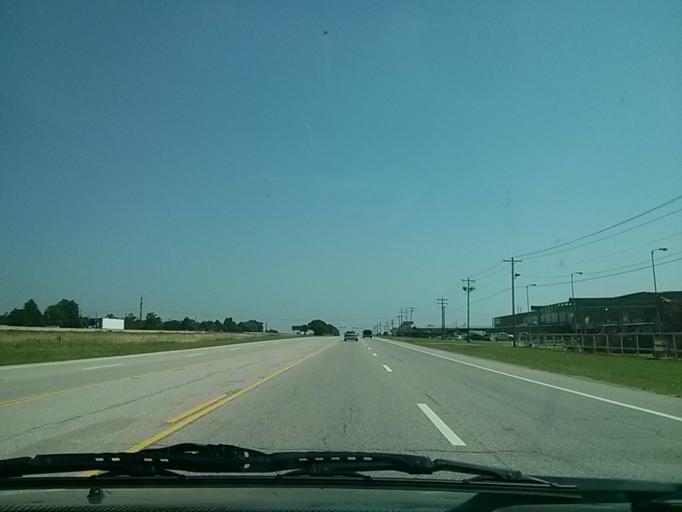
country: US
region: Oklahoma
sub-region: Tulsa County
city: Oakhurst
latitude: 36.0518
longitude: -96.0754
